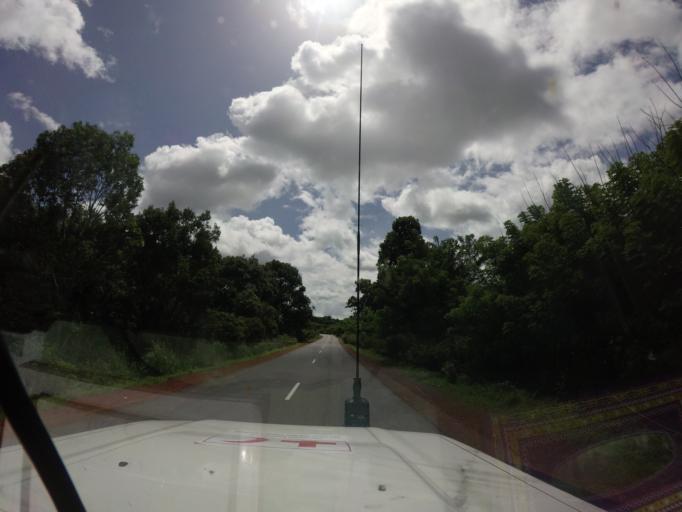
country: SL
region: Northern Province
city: Bindi
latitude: 10.1548
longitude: -11.6878
